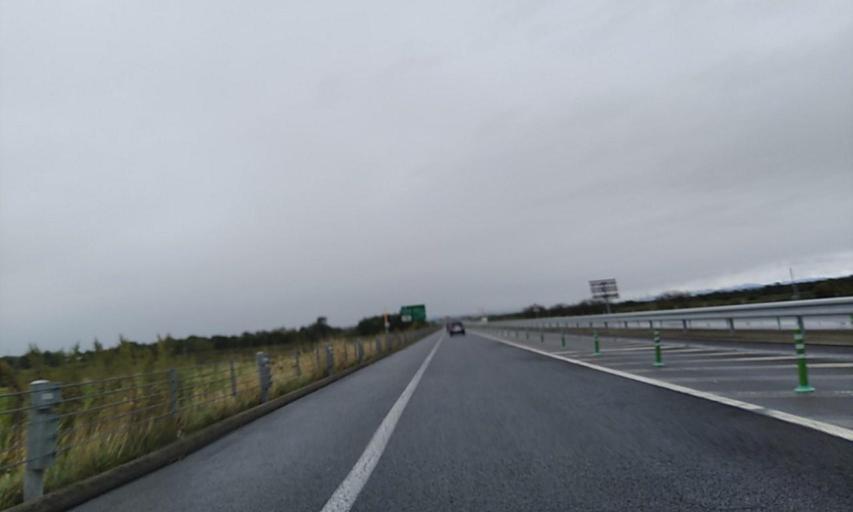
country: JP
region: Hokkaido
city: Kushiro
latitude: 43.0370
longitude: 144.3456
